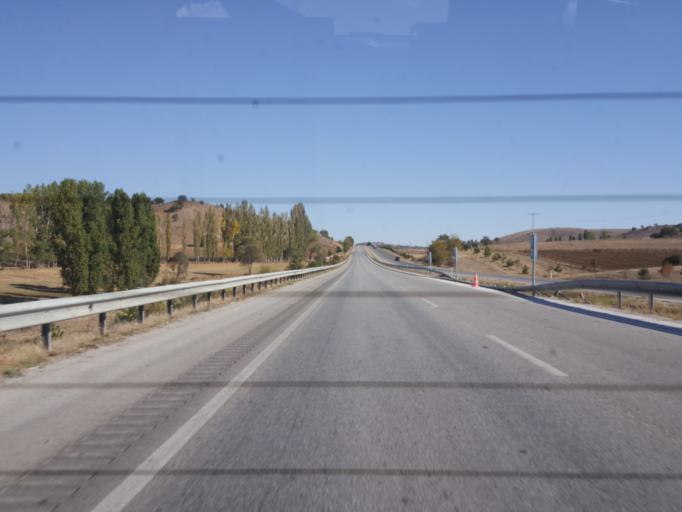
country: TR
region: Corum
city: Alaca
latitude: 40.2812
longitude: 34.6455
